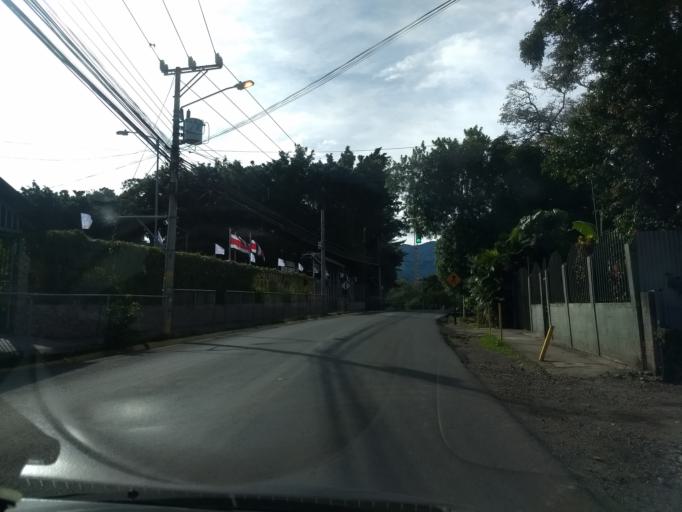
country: CR
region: San Jose
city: Santa Ana
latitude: 9.9479
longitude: -84.1887
